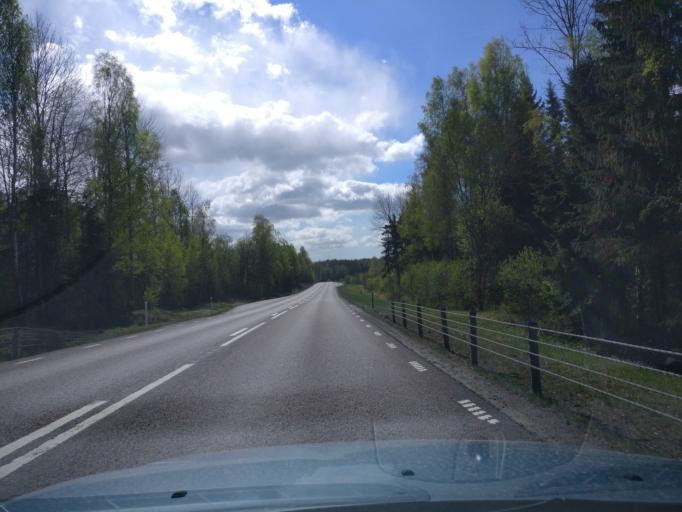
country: SE
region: Vaermland
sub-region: Karlstads Kommun
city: Molkom
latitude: 59.5737
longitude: 13.6676
